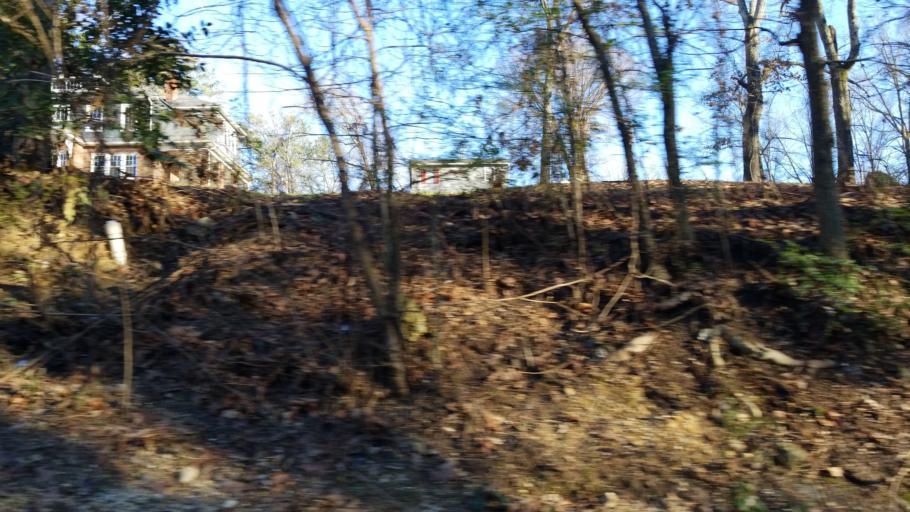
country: US
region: Tennessee
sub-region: Hamilton County
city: East Ridge
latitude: 35.0313
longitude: -85.2458
